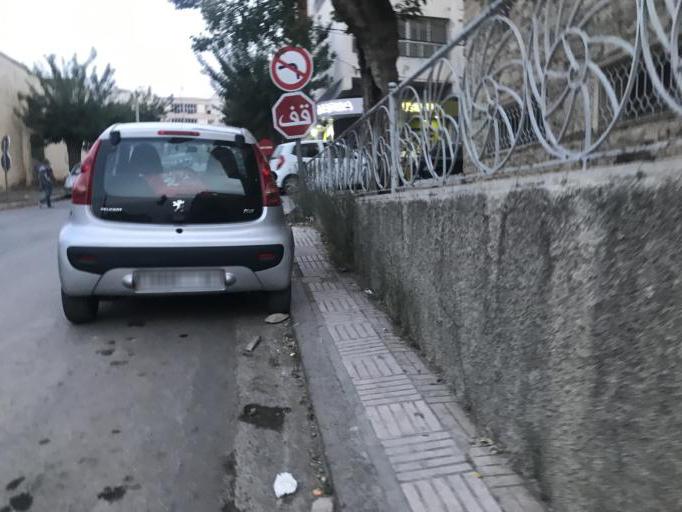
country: MA
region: Taza-Al Hoceima-Taounate
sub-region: Taza
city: Taza
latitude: 34.2246
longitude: -4.0079
